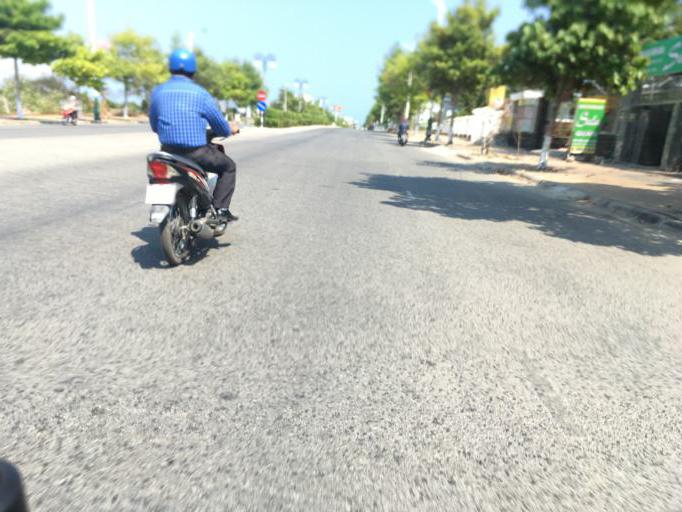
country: VN
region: Ninh Thuan
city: Phan Rang-Thap Cham
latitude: 11.5648
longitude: 109.0037
